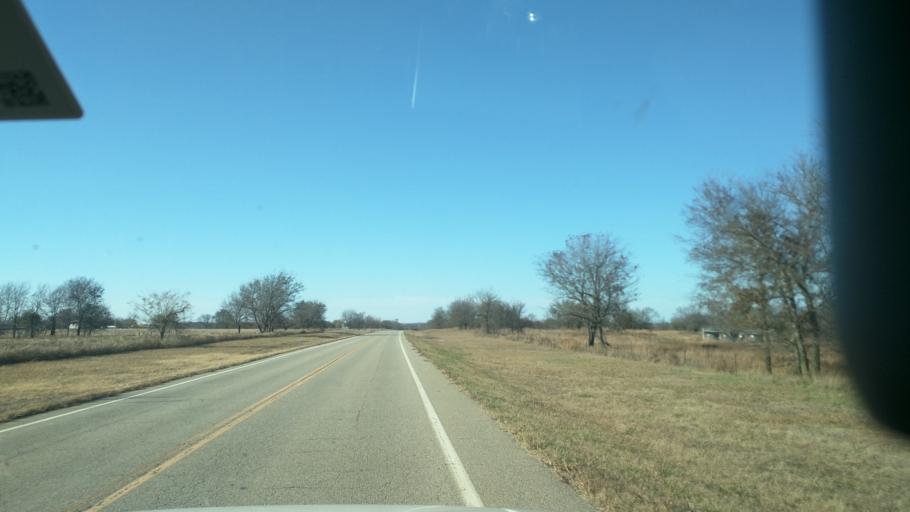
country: US
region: Oklahoma
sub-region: Nowata County
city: Nowata
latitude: 36.7400
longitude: -95.5199
